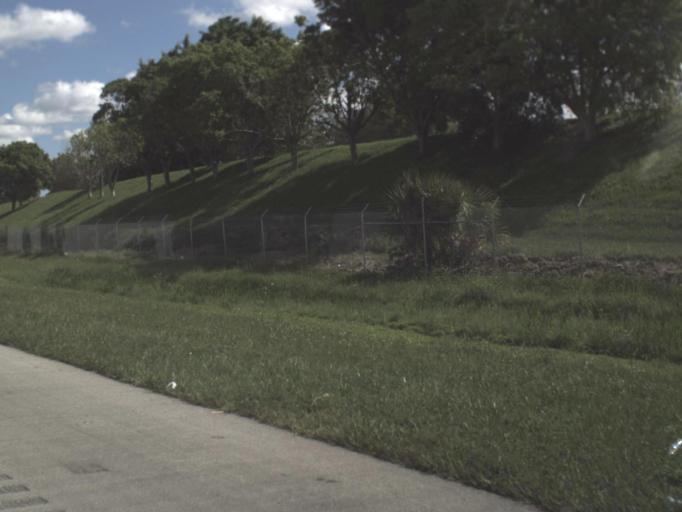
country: US
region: Florida
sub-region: Broward County
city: Coral Springs
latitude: 26.3021
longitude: -80.2900
